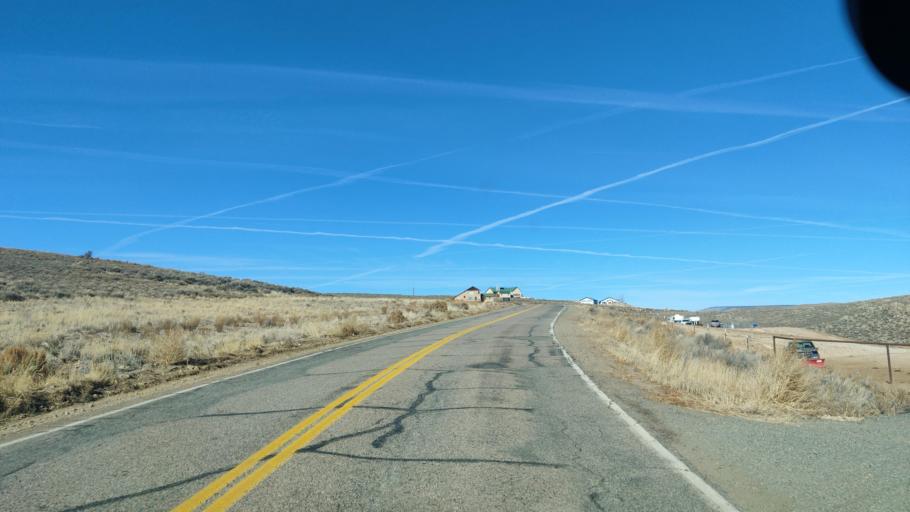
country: US
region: Colorado
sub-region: Gunnison County
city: Gunnison
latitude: 38.5379
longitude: -106.9585
